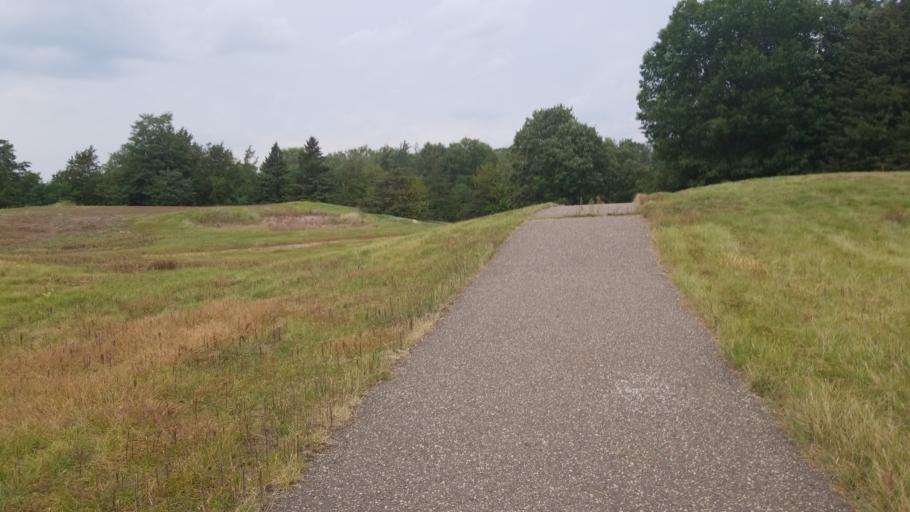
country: US
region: Wisconsin
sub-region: Saint Croix County
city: Hudson
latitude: 44.9714
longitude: -92.7259
